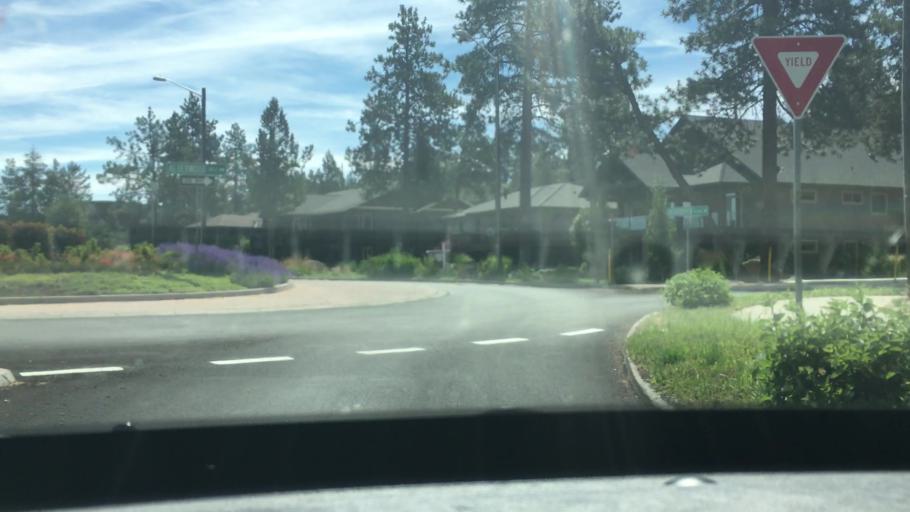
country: US
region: Oregon
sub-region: Deschutes County
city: Bend
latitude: 44.0405
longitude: -121.3220
